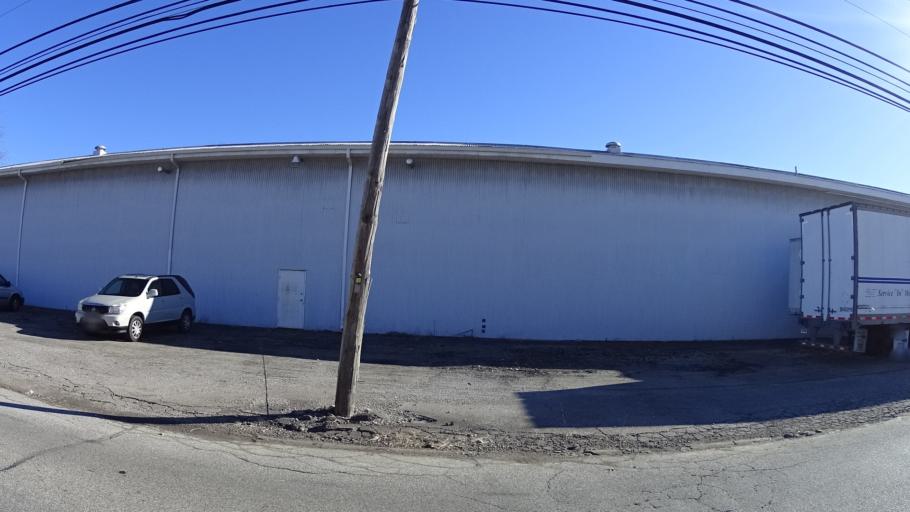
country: US
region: Ohio
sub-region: Lorain County
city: Elyria
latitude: 41.3711
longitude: -82.0708
